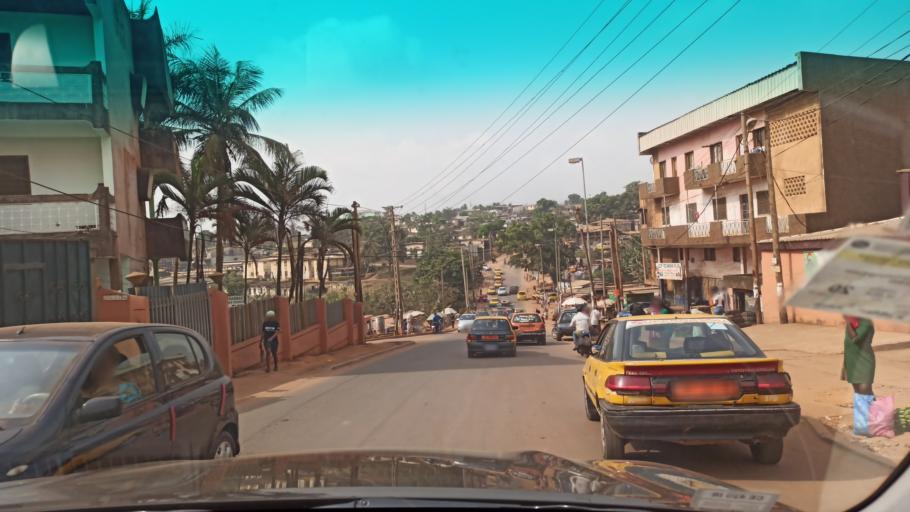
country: CM
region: Centre
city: Yaounde
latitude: 3.8800
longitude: 11.4926
